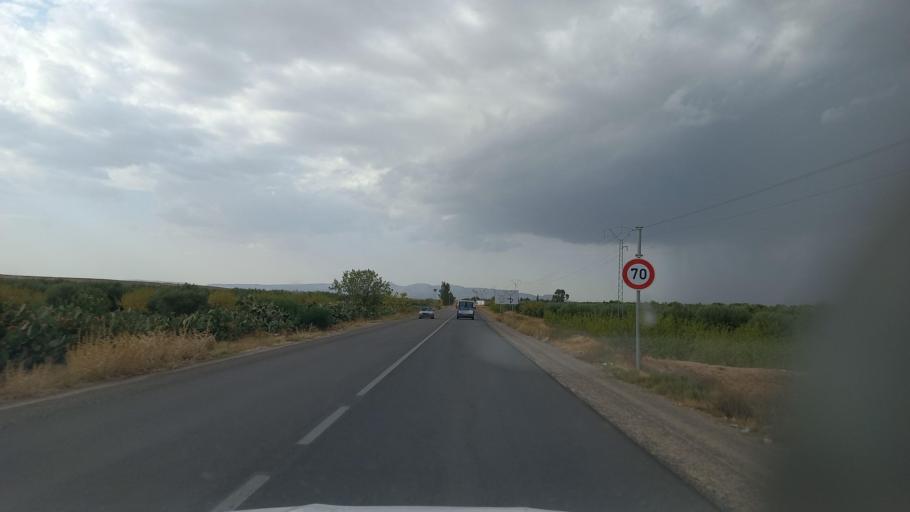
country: TN
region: Al Qasrayn
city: Sbiba
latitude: 35.3058
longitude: 9.0868
